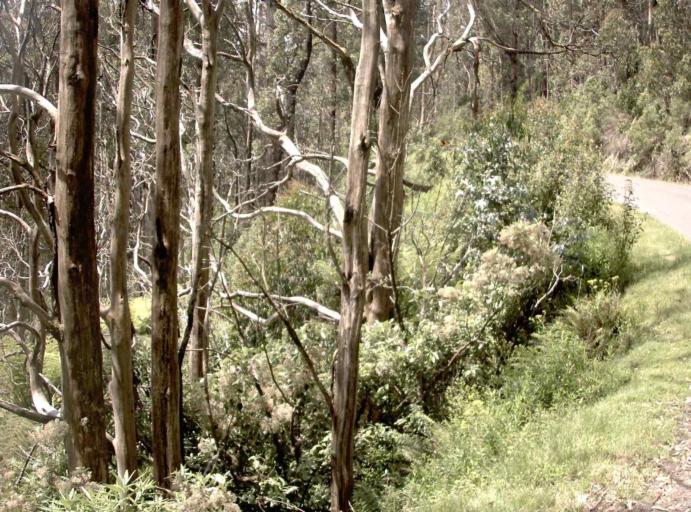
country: AU
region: Victoria
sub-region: Latrobe
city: Traralgon
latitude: -38.4321
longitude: 146.5268
